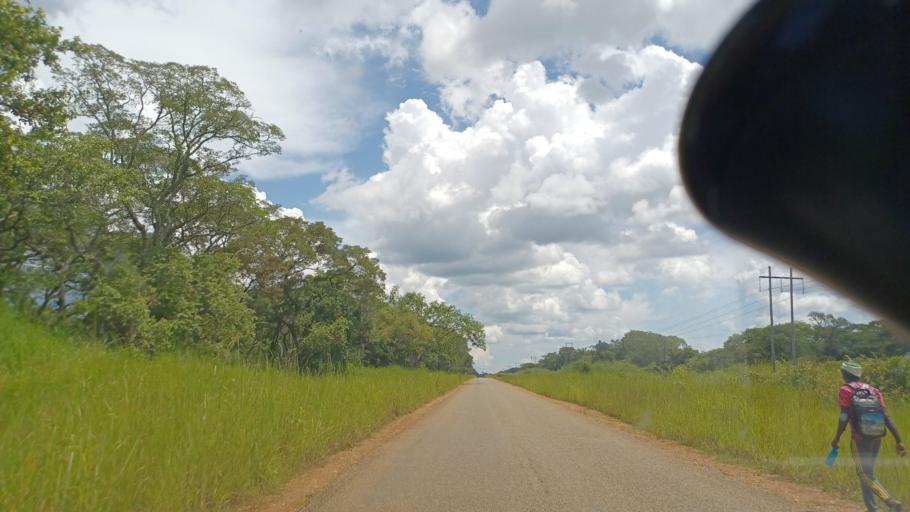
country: ZM
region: North-Western
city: Solwezi
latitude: -12.7063
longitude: 26.0306
